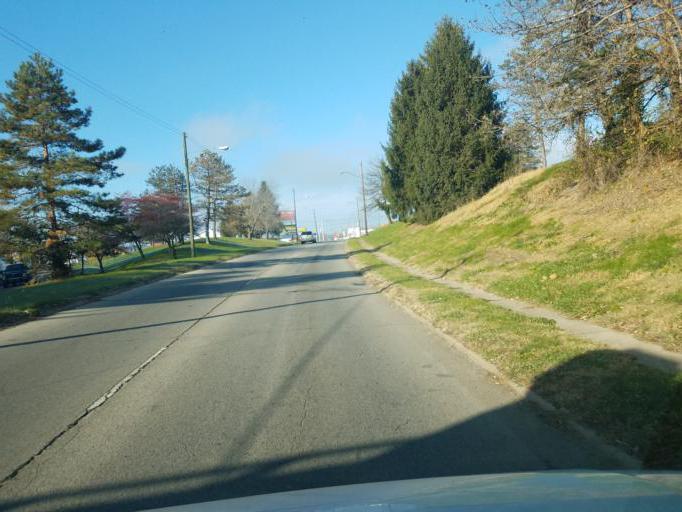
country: US
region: Ohio
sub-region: Scioto County
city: Portsmouth
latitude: 38.7398
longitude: -82.9904
